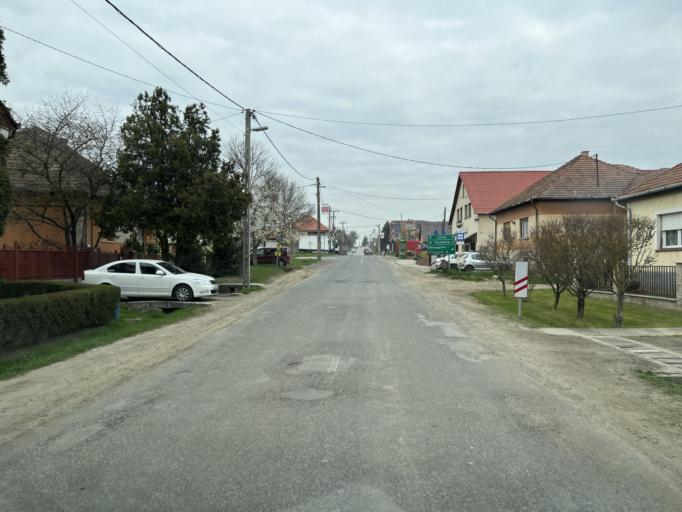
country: HU
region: Pest
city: Acsa
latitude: 47.7965
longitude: 19.3824
